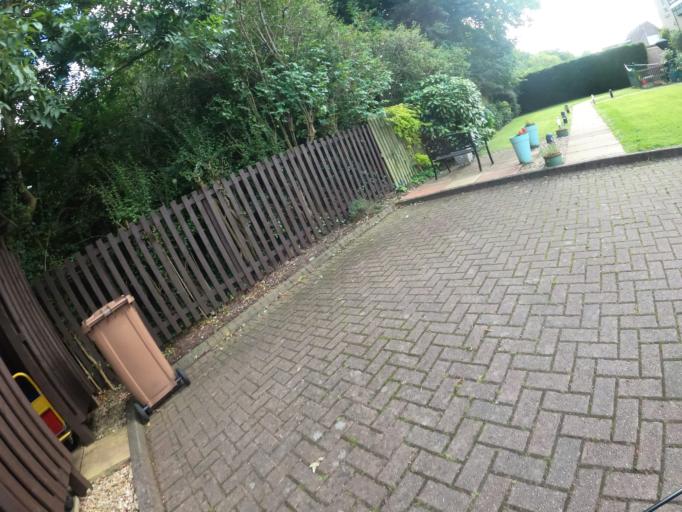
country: GB
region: Scotland
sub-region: Edinburgh
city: Colinton
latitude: 55.9621
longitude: -3.2879
